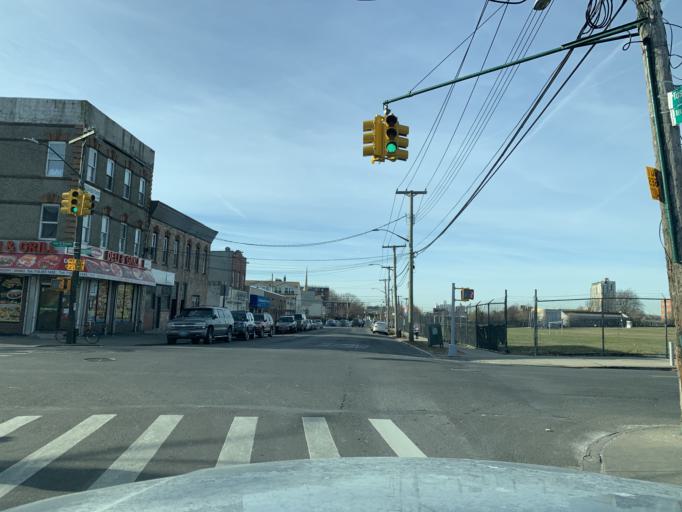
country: US
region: New York
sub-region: Queens County
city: Jamaica
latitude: 40.6998
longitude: -73.7934
